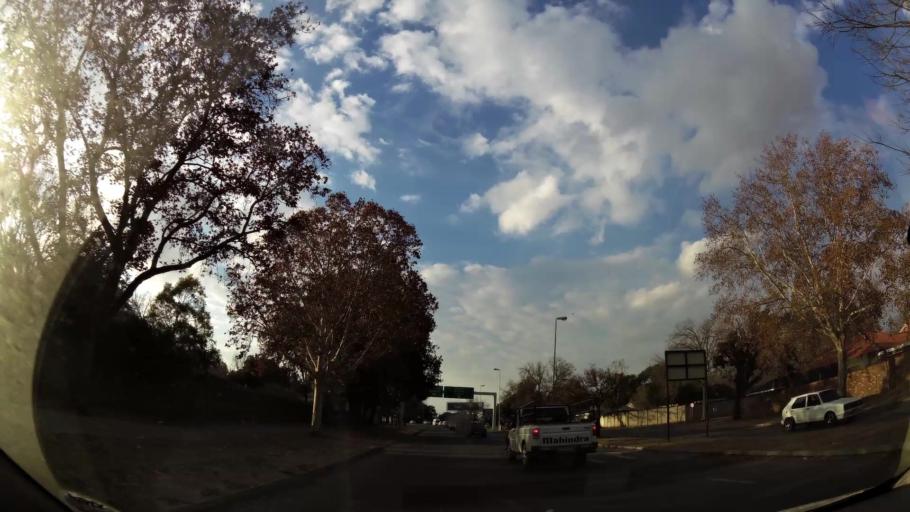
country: ZA
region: Orange Free State
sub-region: Fezile Dabi District Municipality
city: Sasolburg
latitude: -26.8064
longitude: 27.8293
